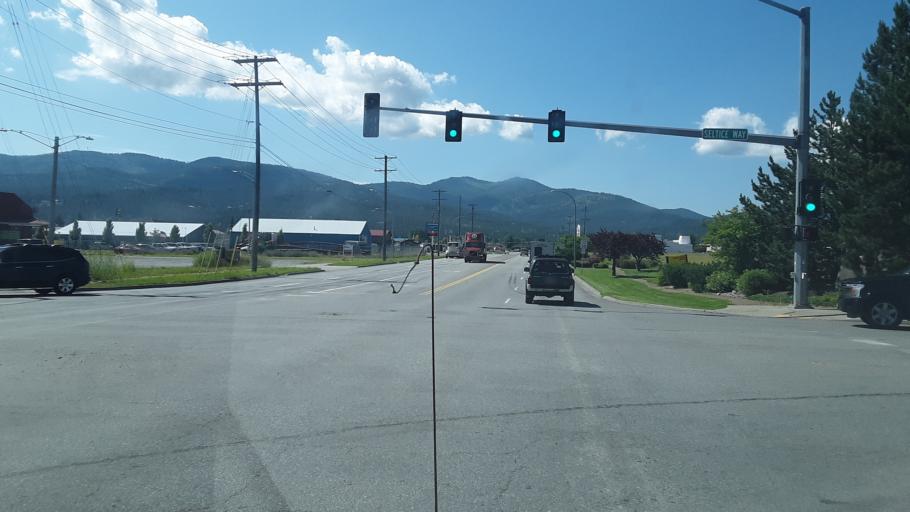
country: US
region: Idaho
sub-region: Kootenai County
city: Post Falls
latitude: 47.7165
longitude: -117.0018
